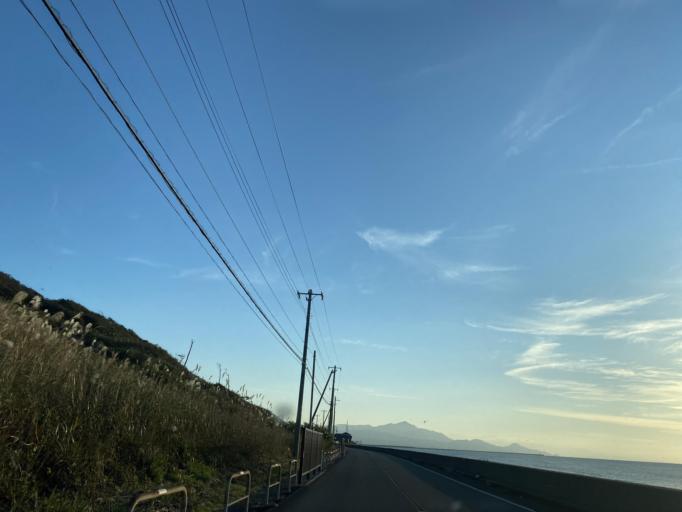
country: JP
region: Niigata
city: Kashiwazaki
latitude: 37.4649
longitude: 138.6137
